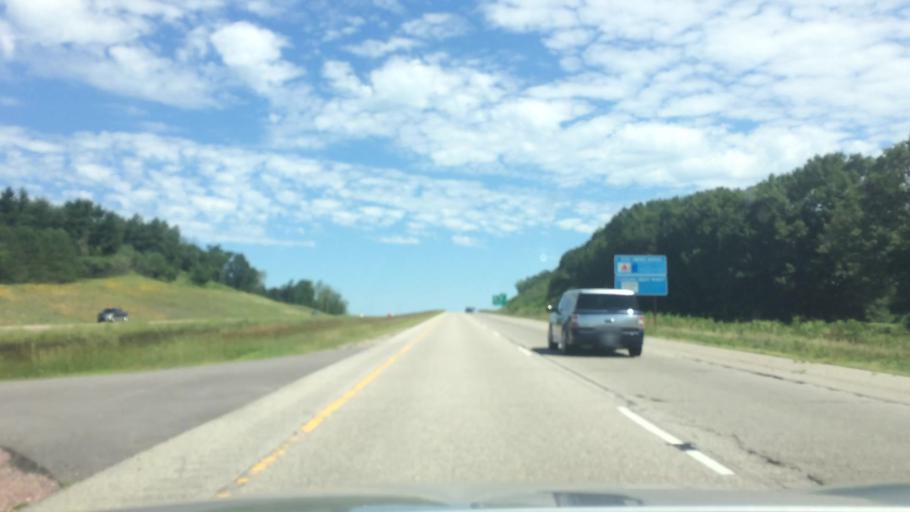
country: US
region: Wisconsin
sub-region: Marquette County
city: Westfield
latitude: 43.7820
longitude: -89.4838
